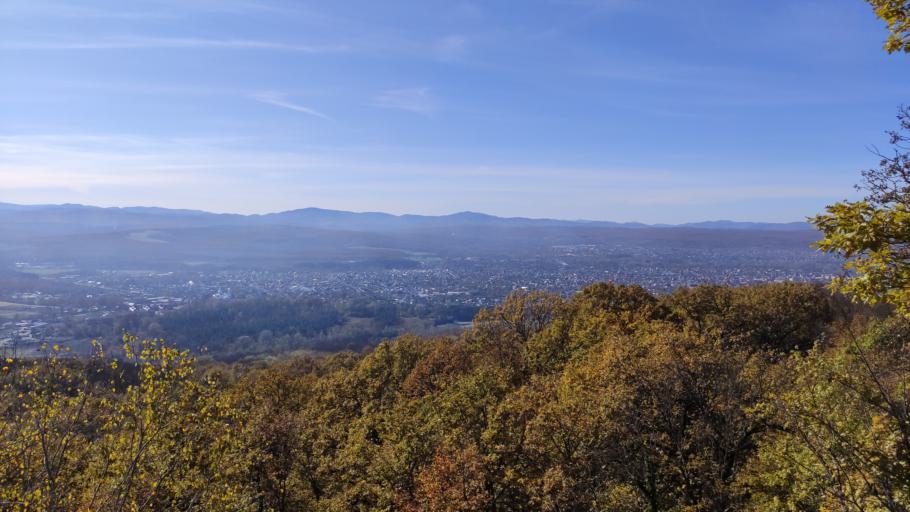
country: RU
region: Krasnodarskiy
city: Apsheronsk
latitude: 44.4600
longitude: 39.7806
